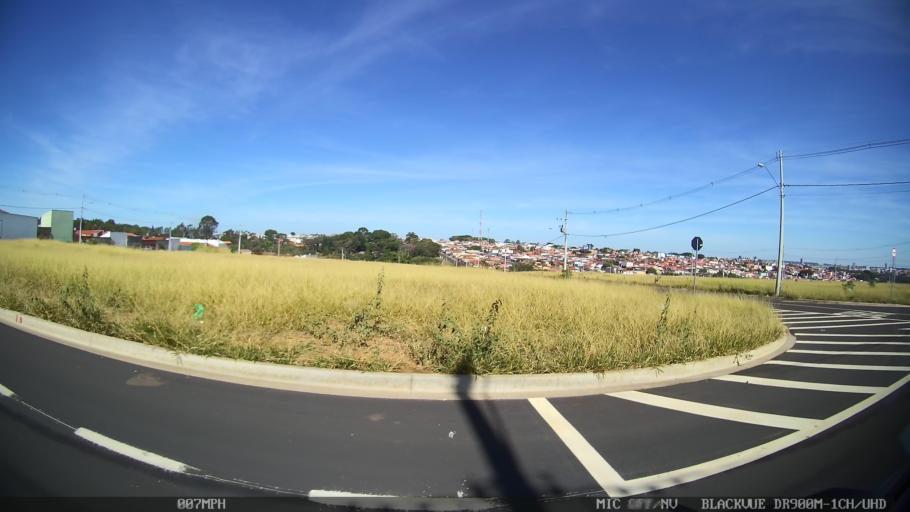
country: BR
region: Sao Paulo
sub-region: Franca
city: Franca
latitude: -20.5542
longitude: -47.3654
